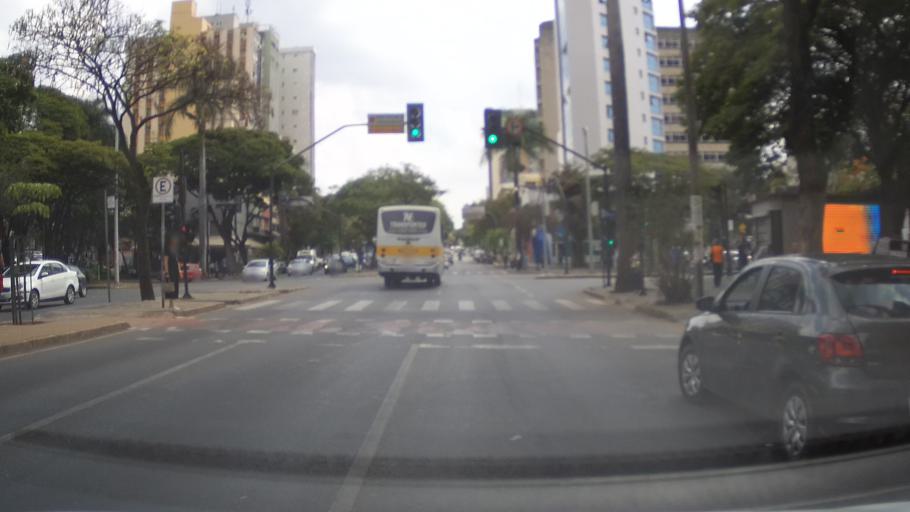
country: BR
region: Minas Gerais
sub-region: Belo Horizonte
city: Belo Horizonte
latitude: -19.9260
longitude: -43.9250
